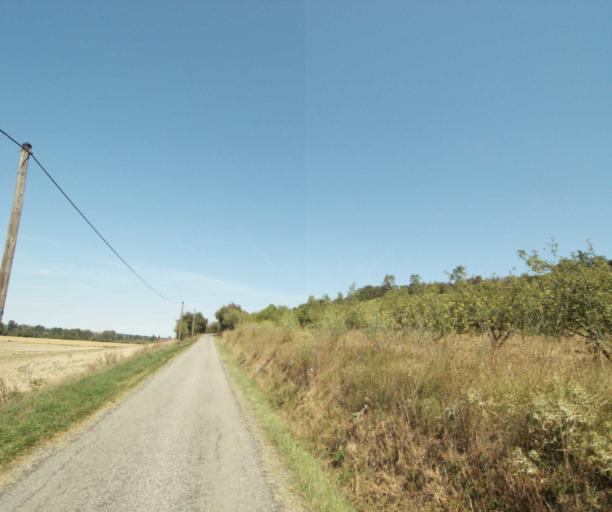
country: FR
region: Midi-Pyrenees
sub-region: Departement de l'Ariege
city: Lezat-sur-Leze
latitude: 43.2999
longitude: 1.3480
